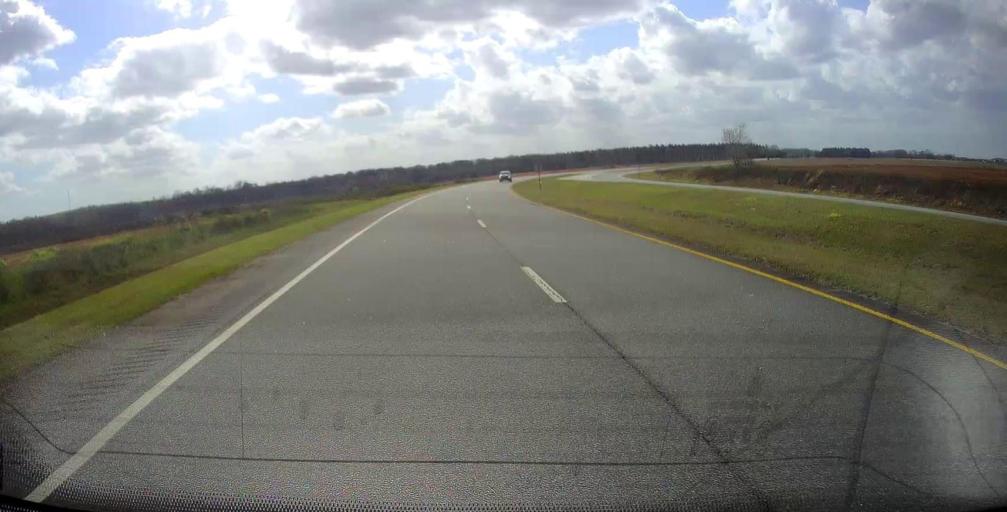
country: US
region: Georgia
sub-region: Houston County
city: Perry
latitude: 32.4313
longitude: -83.7224
